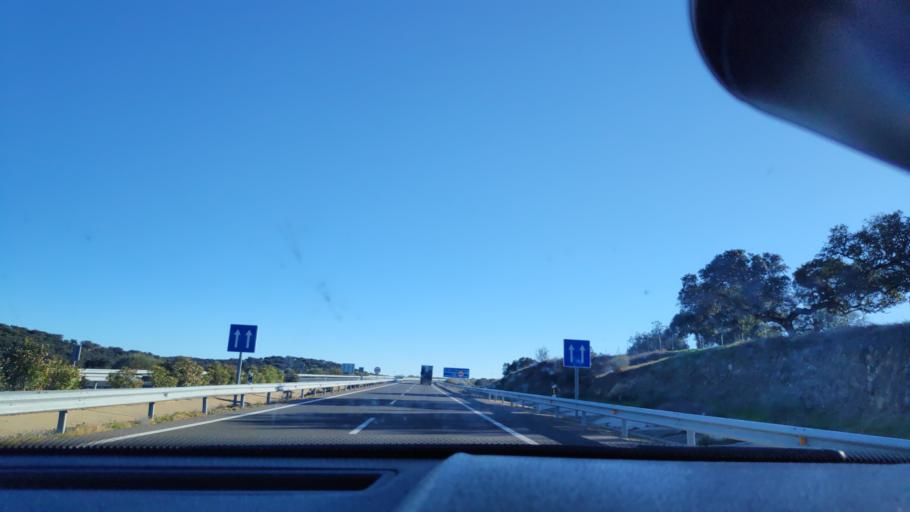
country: ES
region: Extremadura
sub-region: Provincia de Badajoz
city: Monesterio
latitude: 38.1276
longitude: -6.2721
